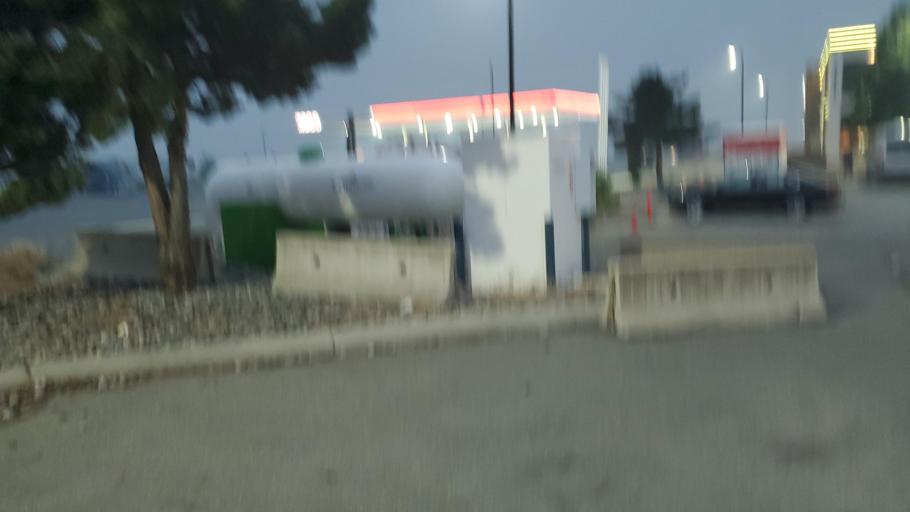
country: CA
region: British Columbia
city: Merritt
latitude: 50.1242
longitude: -120.7483
